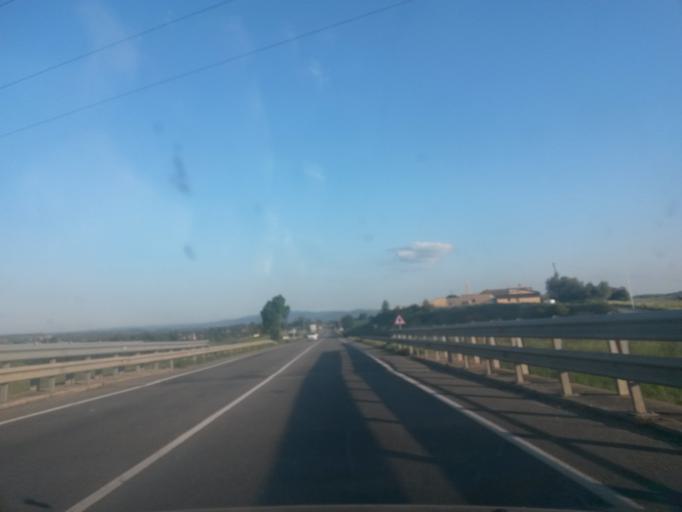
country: ES
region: Catalonia
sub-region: Provincia de Girona
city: Fontcoberta
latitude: 42.1220
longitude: 2.7849
